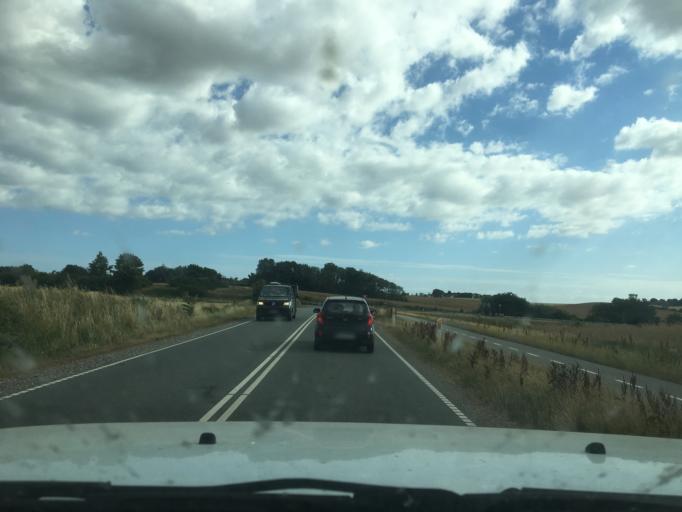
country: DK
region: Central Jutland
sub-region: Arhus Kommune
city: Logten
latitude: 56.2893
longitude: 10.3123
